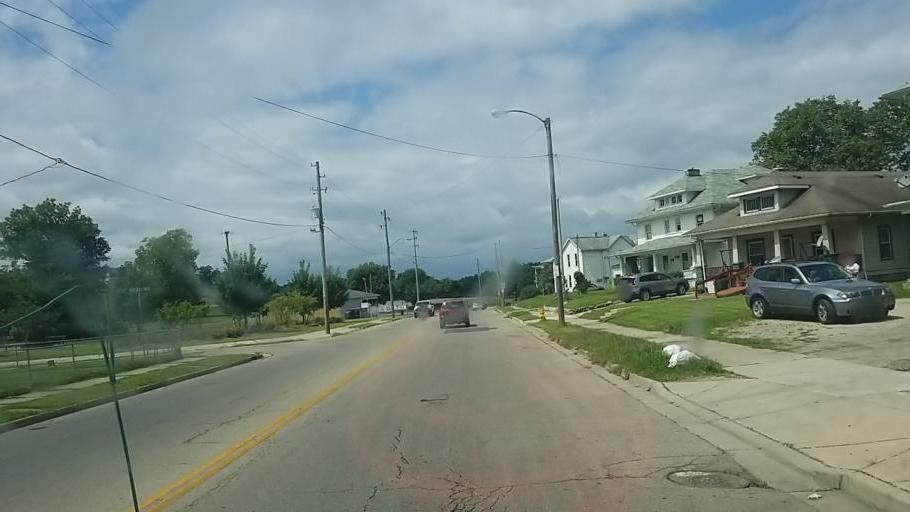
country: US
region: Ohio
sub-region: Clark County
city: Springfield
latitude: 39.9162
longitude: -83.8050
